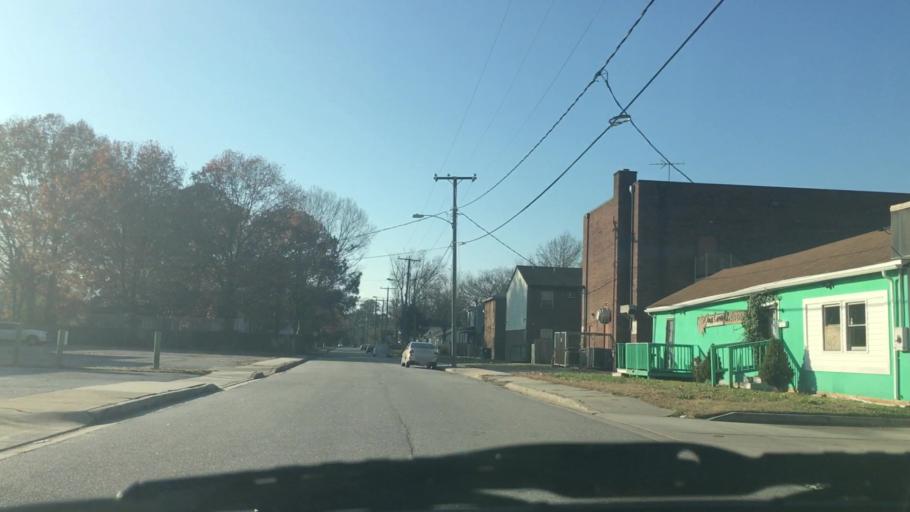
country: US
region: Virginia
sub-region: City of Norfolk
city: Norfolk
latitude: 36.8905
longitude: -76.2393
